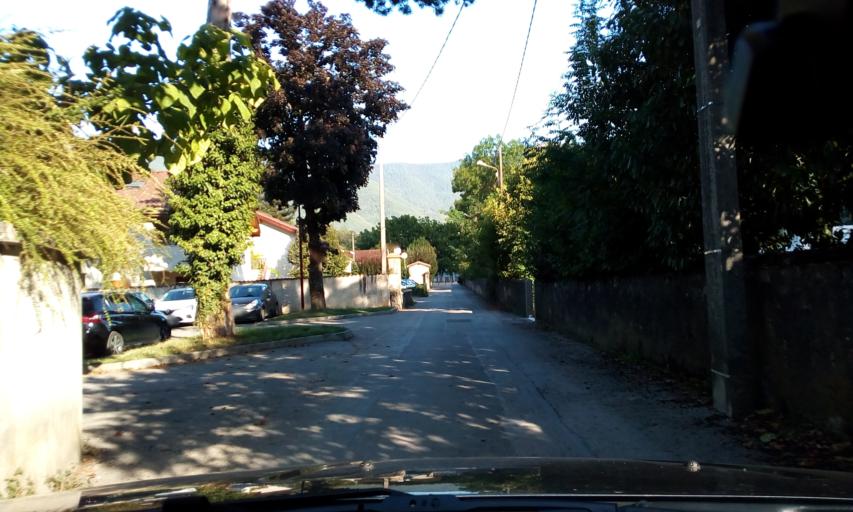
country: FR
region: Rhone-Alpes
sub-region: Departement de l'Isere
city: Vif
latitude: 45.0536
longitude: 5.6706
